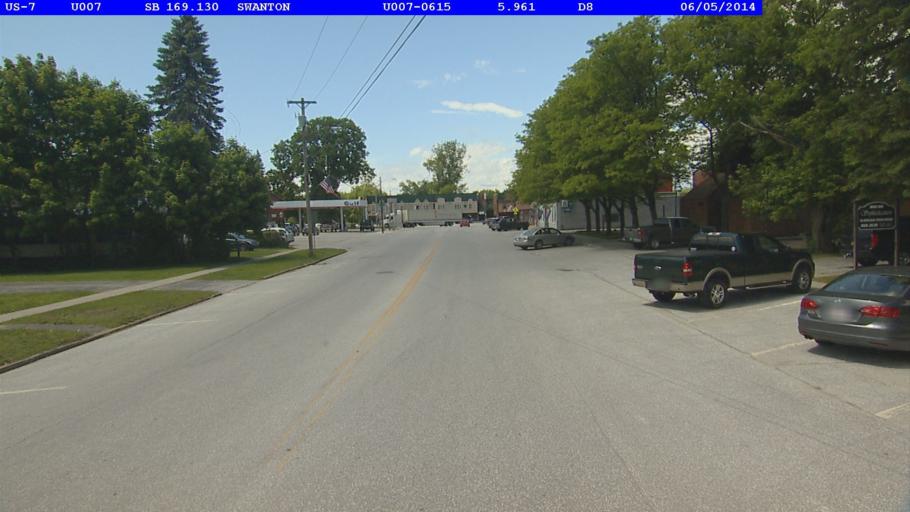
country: US
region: Vermont
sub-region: Franklin County
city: Swanton
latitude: 44.9199
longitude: -73.1238
